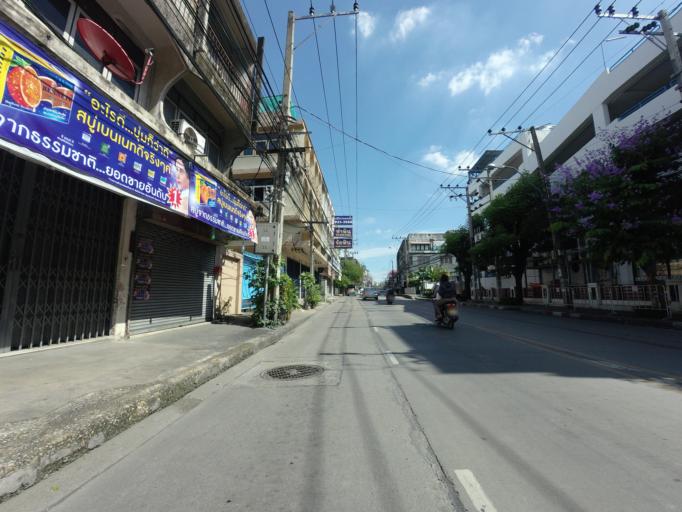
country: TH
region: Bangkok
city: Lat Phrao
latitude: 13.8017
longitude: 100.5964
